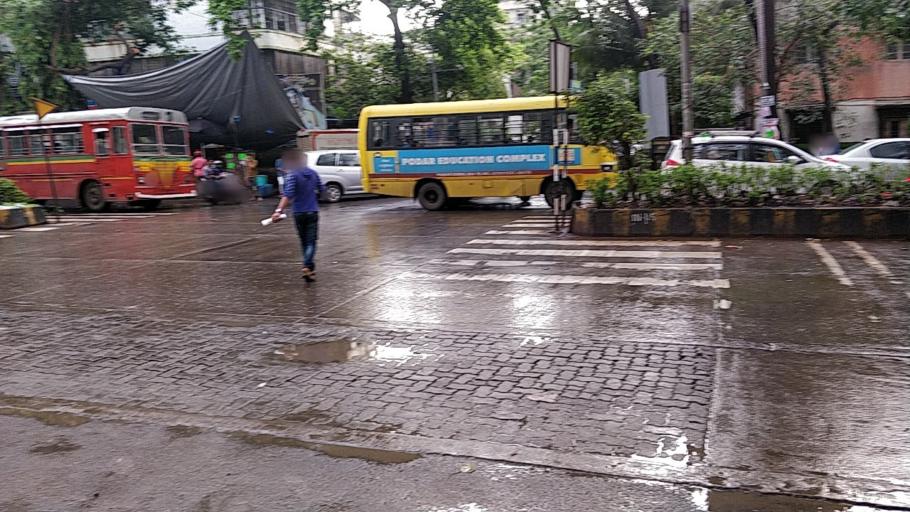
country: IN
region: Maharashtra
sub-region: Mumbai Suburban
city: Mumbai
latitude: 19.1046
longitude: 72.8369
